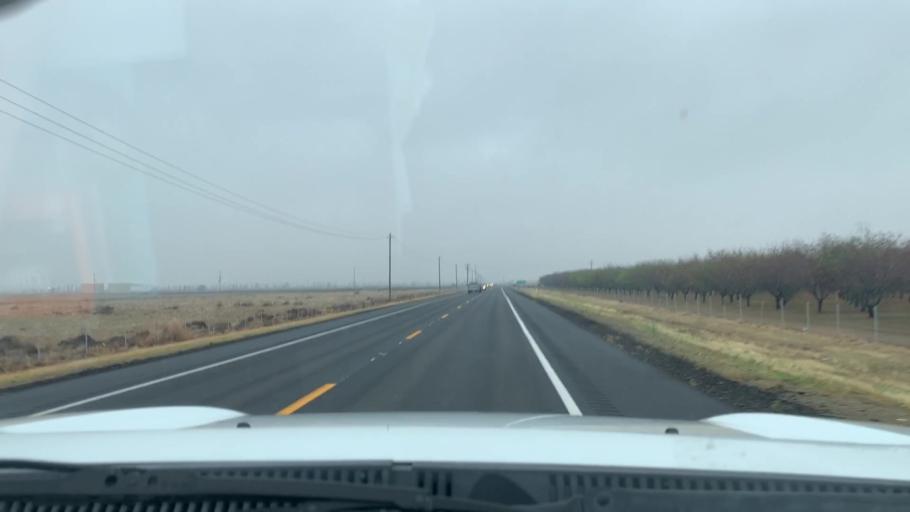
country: US
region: California
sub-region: Kern County
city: Lost Hills
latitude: 35.6157
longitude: -119.7492
